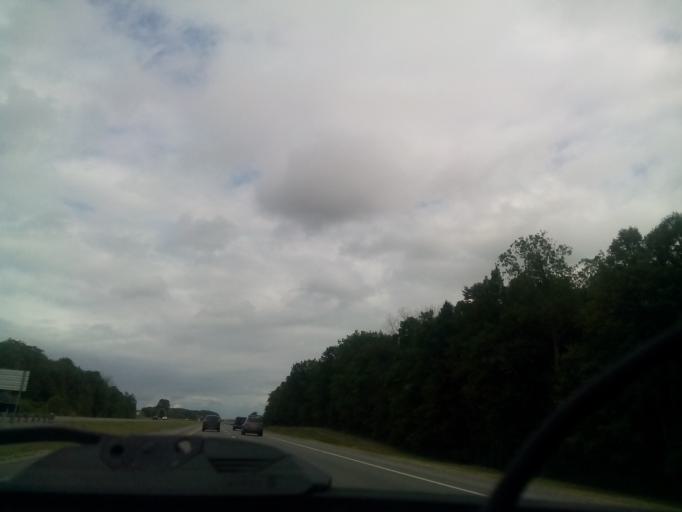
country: US
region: Ohio
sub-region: Williams County
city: Montpelier
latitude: 41.6278
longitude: -84.7272
